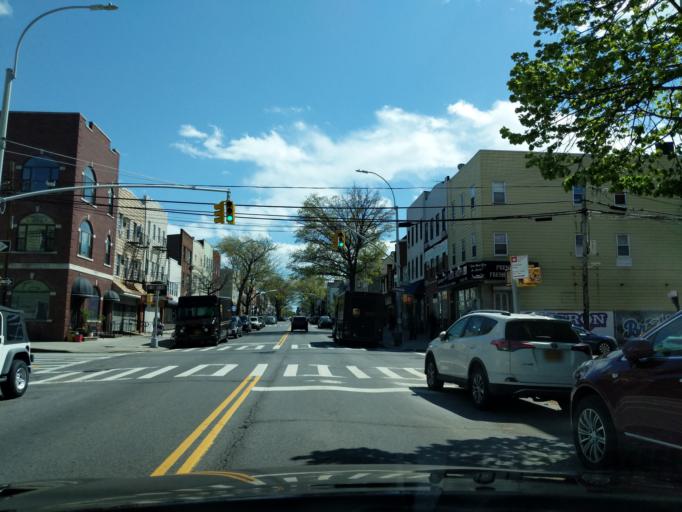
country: US
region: New York
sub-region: Queens County
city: Long Island City
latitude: 40.7183
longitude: -73.9450
